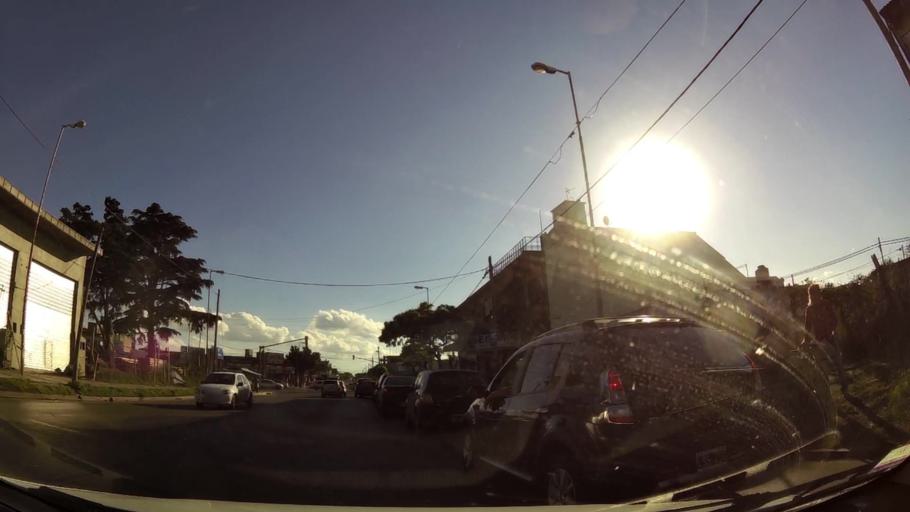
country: AR
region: Buenos Aires
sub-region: Partido de Moron
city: Moron
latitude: -34.6933
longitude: -58.6304
